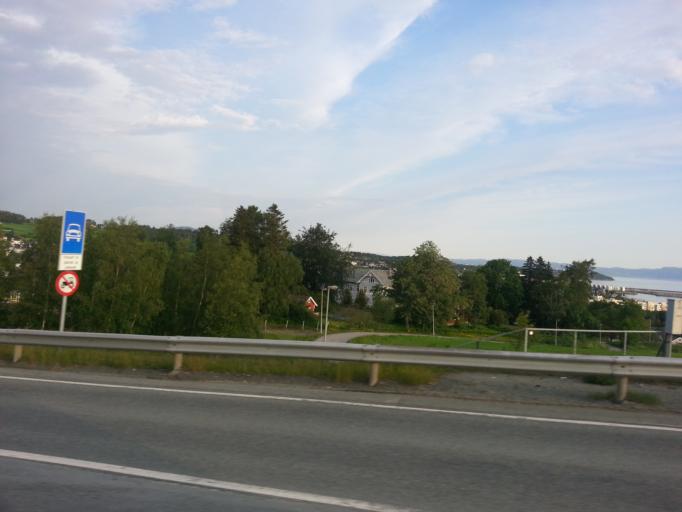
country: NO
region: Sor-Trondelag
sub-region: Klaebu
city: Klaebu
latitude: 63.4234
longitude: 10.5411
